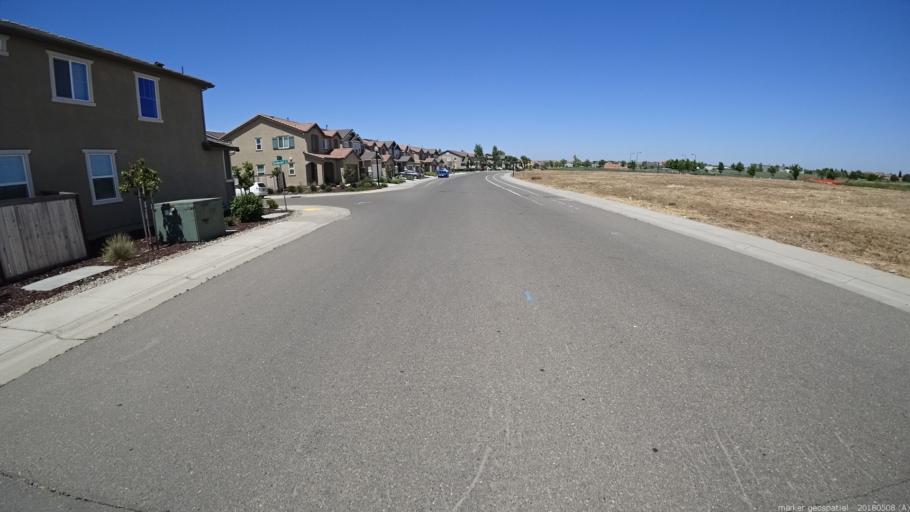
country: US
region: California
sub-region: Sacramento County
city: Elverta
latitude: 38.6719
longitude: -121.5304
